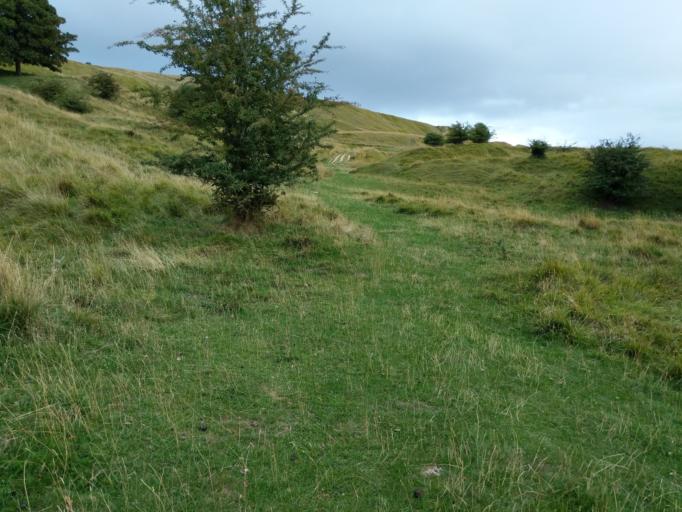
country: GB
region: England
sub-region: Gloucestershire
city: Gotherington
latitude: 51.9386
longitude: -2.0275
